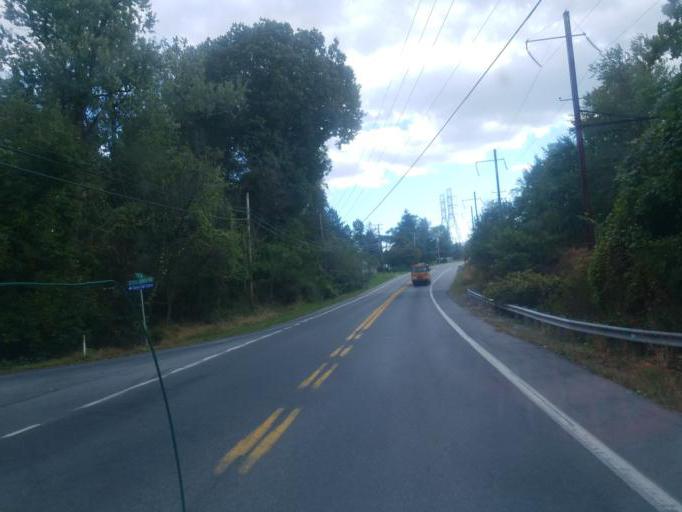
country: US
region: Pennsylvania
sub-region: Dauphin County
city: Middletown
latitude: 40.1649
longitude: -76.7185
